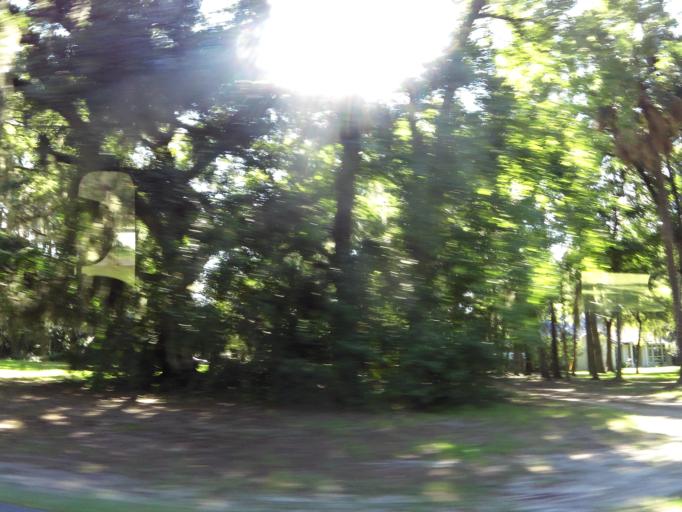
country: US
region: Florida
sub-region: Nassau County
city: Fernandina Beach
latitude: 30.6411
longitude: -81.4630
